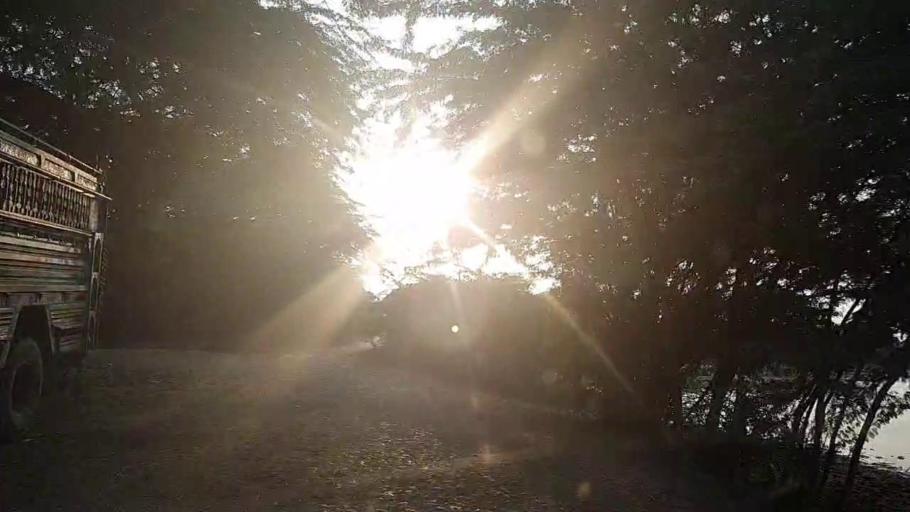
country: PK
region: Sindh
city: Mirpur Sakro
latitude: 24.5533
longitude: 67.5698
